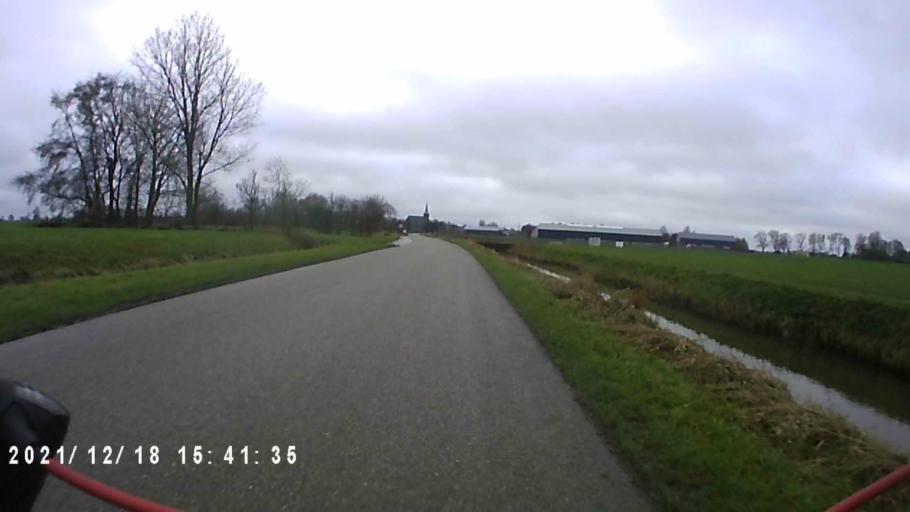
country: NL
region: Friesland
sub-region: Gemeente Dongeradeel
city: Anjum
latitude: 53.3353
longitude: 6.1067
